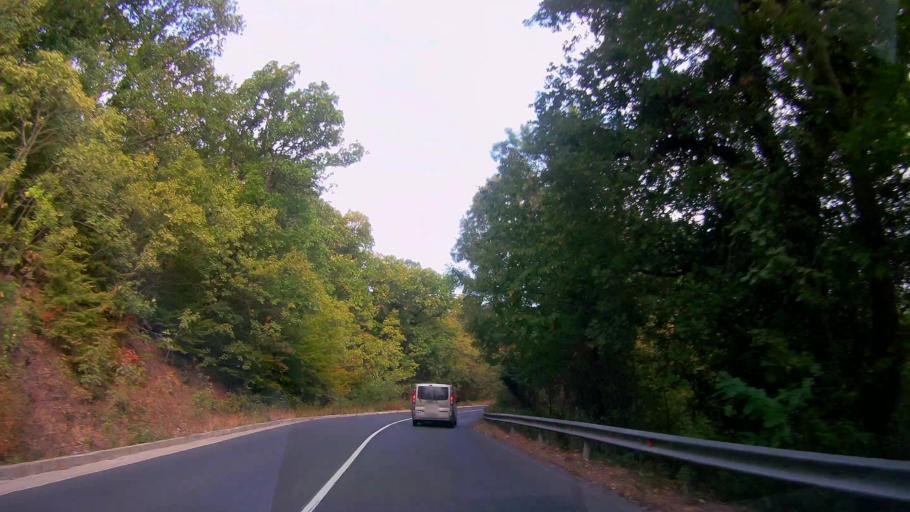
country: BG
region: Burgas
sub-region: Obshtina Primorsko
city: Primorsko
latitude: 42.3208
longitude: 27.7305
